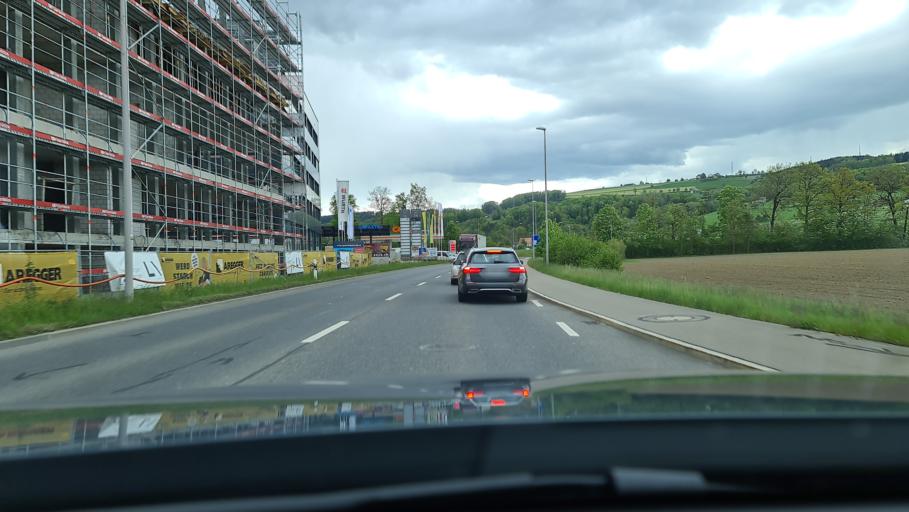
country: CH
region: Lucerne
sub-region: Sursee District
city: Sursee
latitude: 47.1832
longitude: 8.1116
